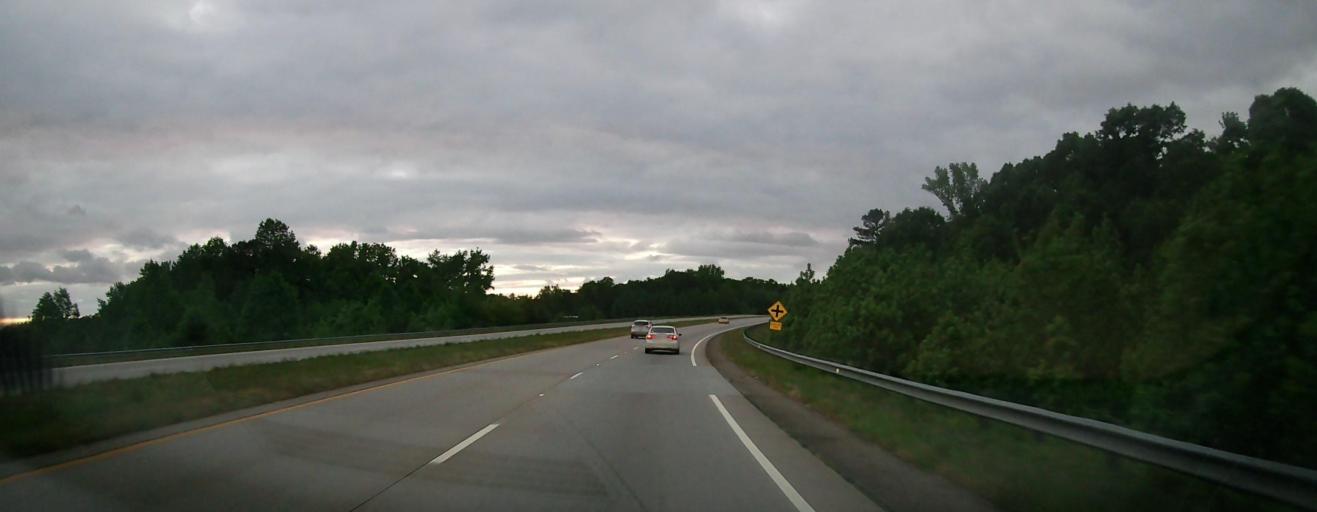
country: US
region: Georgia
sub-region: Jackson County
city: Arcade
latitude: 34.0753
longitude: -83.5712
